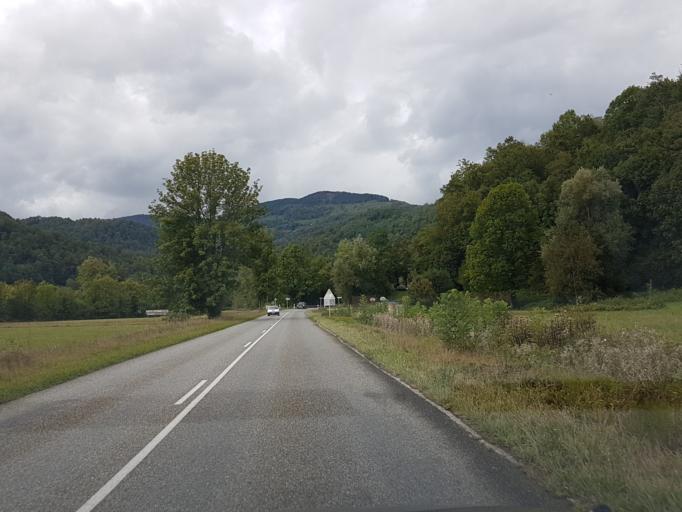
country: FR
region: Midi-Pyrenees
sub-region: Departement de l'Ariege
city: Saint-Girons
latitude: 42.8898
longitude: 1.2148
